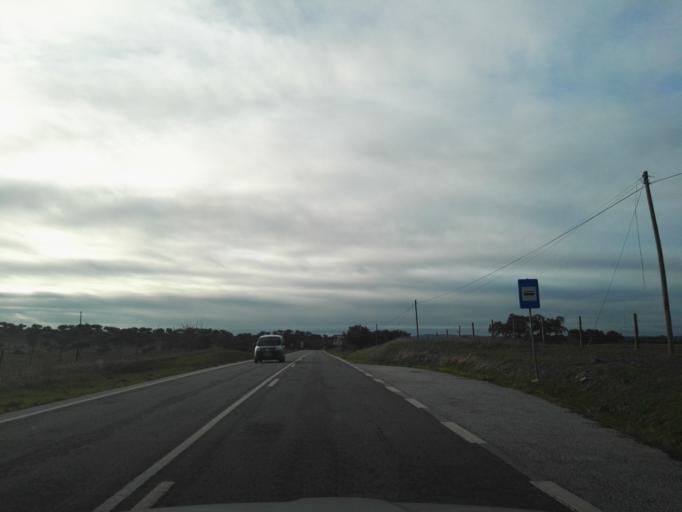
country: PT
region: Evora
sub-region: Redondo
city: Redondo
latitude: 38.6520
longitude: -7.6749
